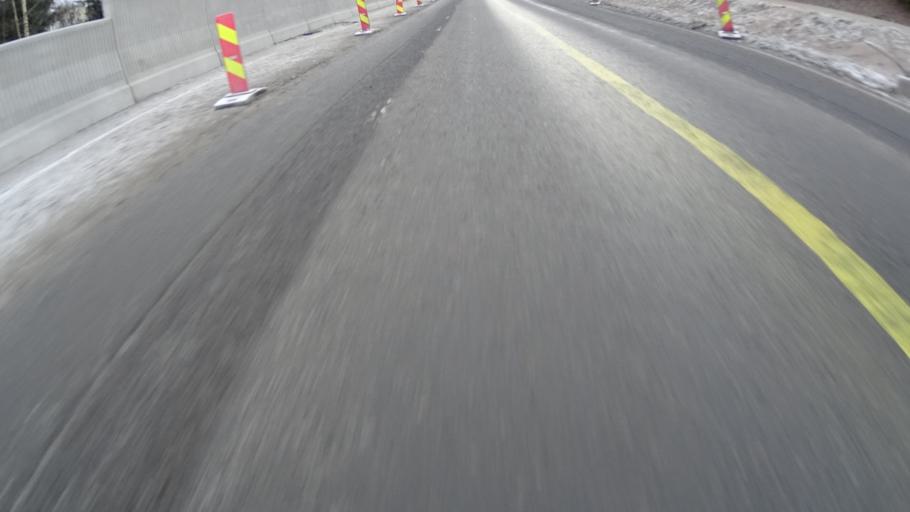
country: FI
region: Uusimaa
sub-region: Helsinki
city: Nurmijaervi
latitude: 60.3882
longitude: 24.7426
